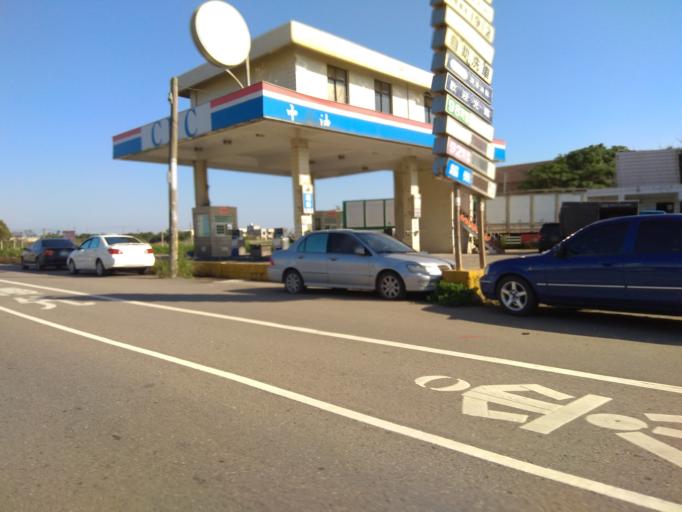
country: TW
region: Taiwan
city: Taoyuan City
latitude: 25.0533
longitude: 121.1549
